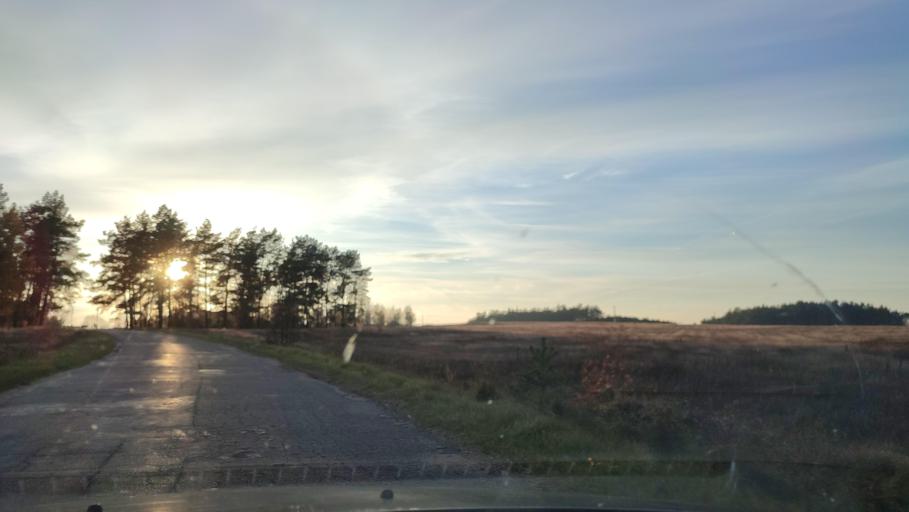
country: PL
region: Masovian Voivodeship
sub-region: Powiat mlawski
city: Dzierzgowo
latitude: 53.2639
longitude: 20.6259
